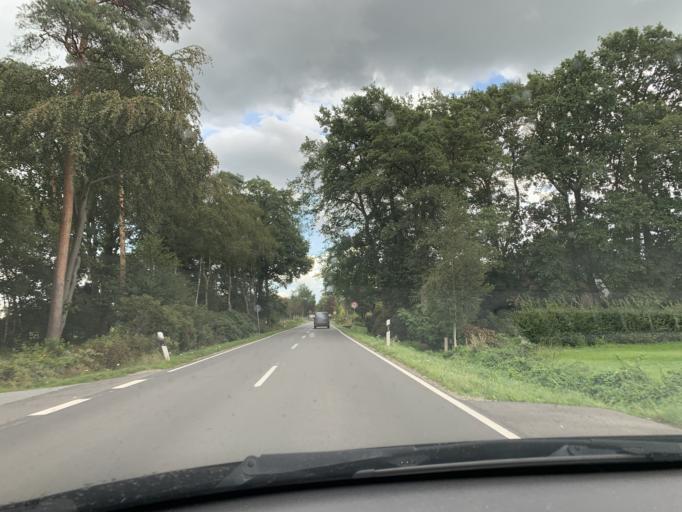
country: DE
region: Lower Saxony
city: Westerstede
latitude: 53.2865
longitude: 8.0197
